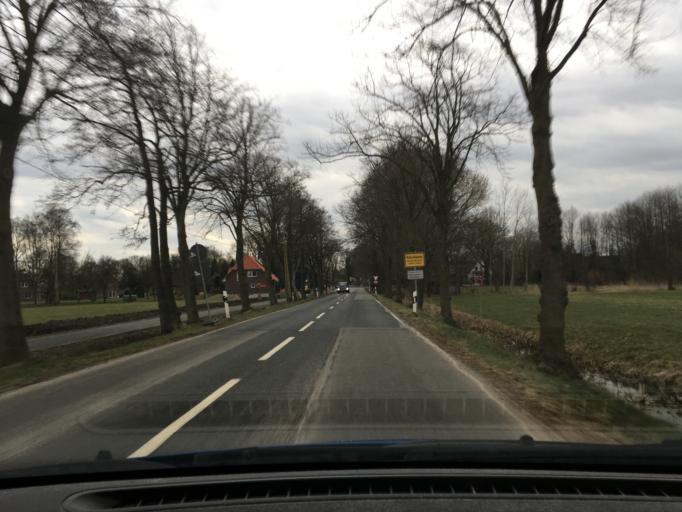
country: DE
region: Lower Saxony
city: Handorf
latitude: 53.3694
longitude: 10.3332
